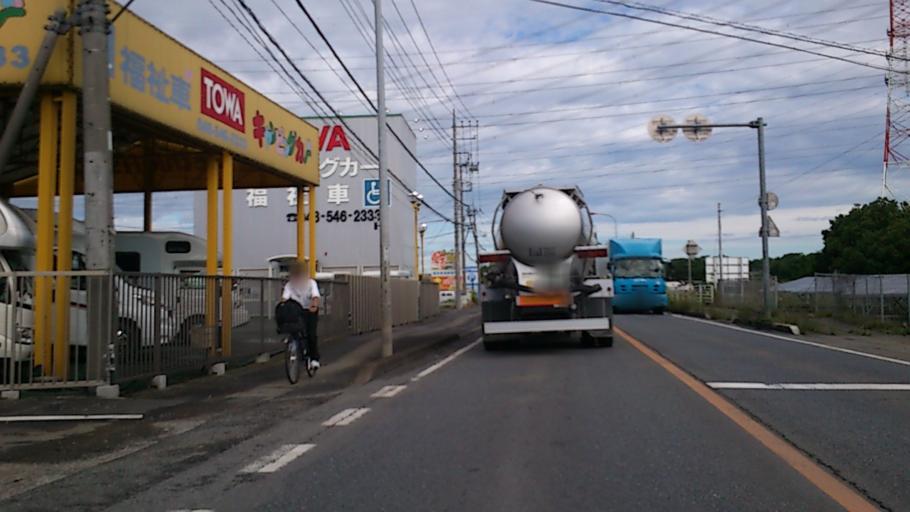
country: JP
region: Saitama
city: Honjo
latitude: 36.2249
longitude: 139.2232
